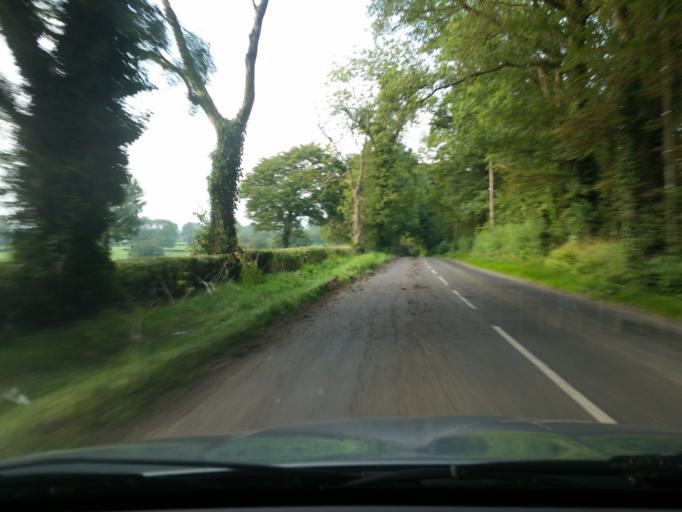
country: GB
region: Northern Ireland
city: Lisnaskea
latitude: 54.2867
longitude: -7.4253
